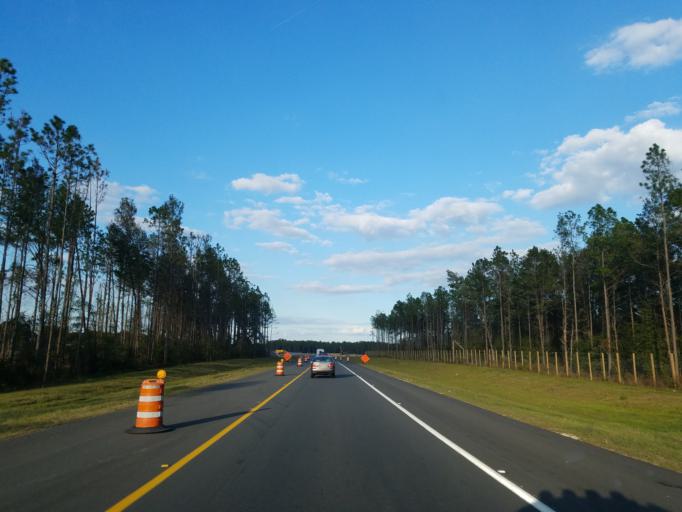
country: US
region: Florida
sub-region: Hernando County
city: Hill 'n Dale
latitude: 28.5112
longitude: -82.2406
